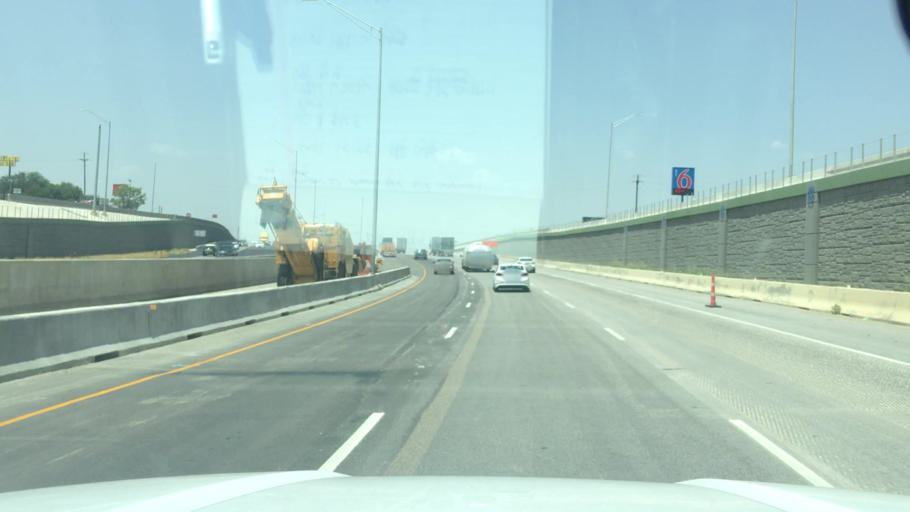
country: US
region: Texas
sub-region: Tarrant County
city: Euless
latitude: 32.8389
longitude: -97.0831
